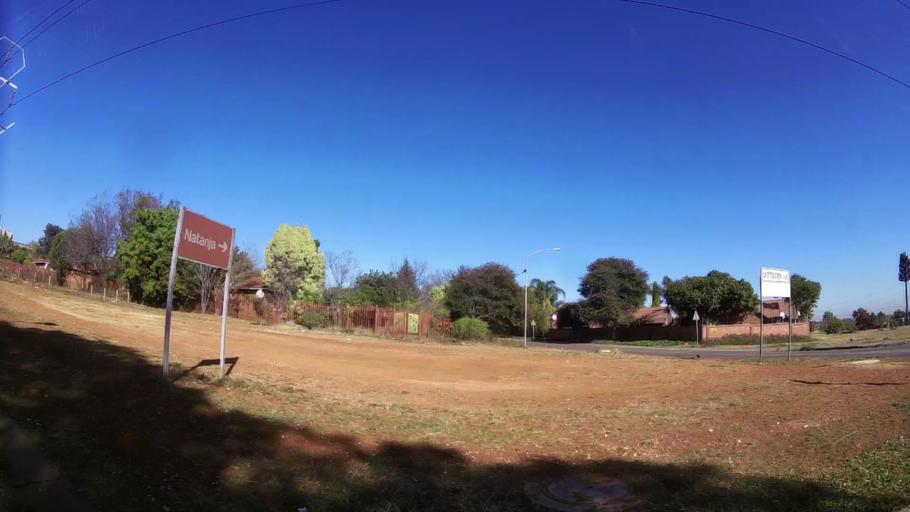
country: ZA
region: Gauteng
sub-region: City of Tshwane Metropolitan Municipality
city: Centurion
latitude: -25.8288
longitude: 28.1956
